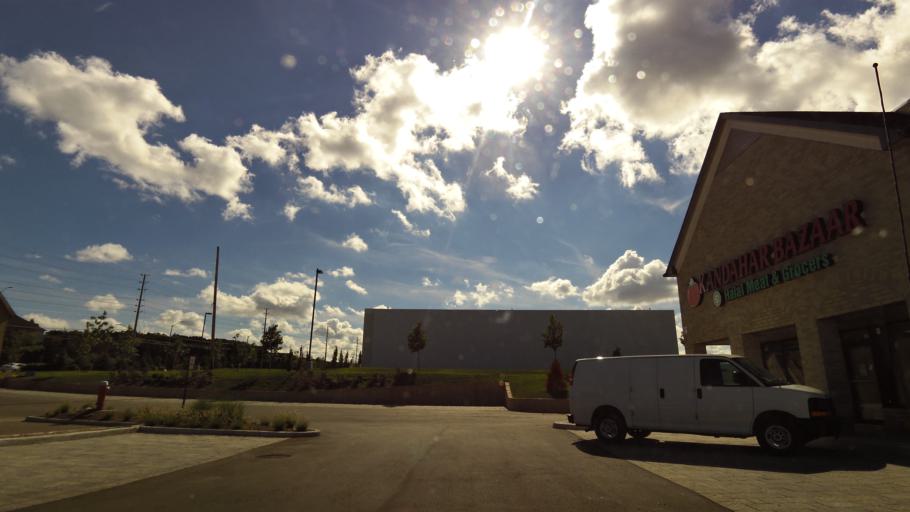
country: CA
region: Ontario
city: Mississauga
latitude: 43.5829
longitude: -79.7297
